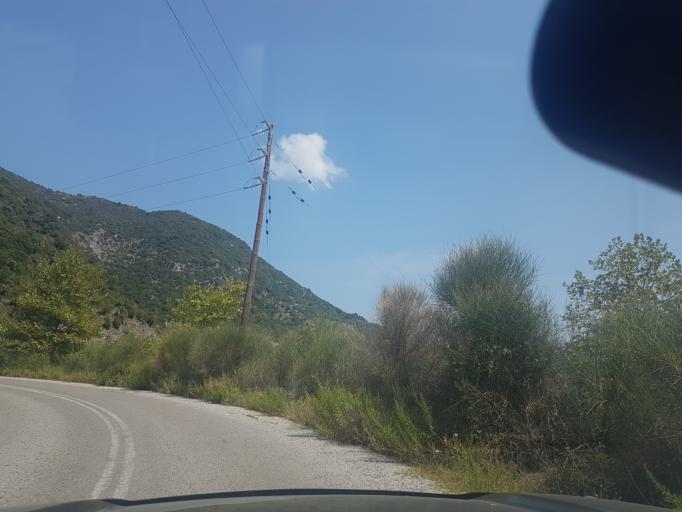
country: GR
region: Central Greece
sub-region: Nomos Evvoias
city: Yimnon
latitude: 38.6354
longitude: 23.8909
